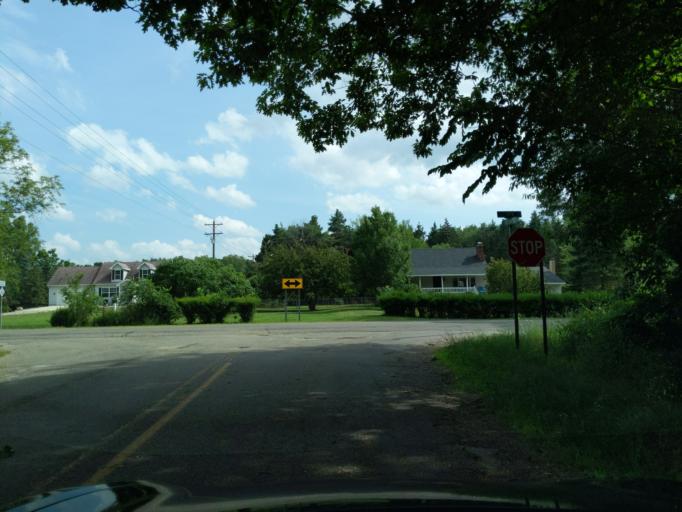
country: US
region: Michigan
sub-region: Eaton County
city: Eaton Rapids
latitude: 42.4948
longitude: -84.6305
